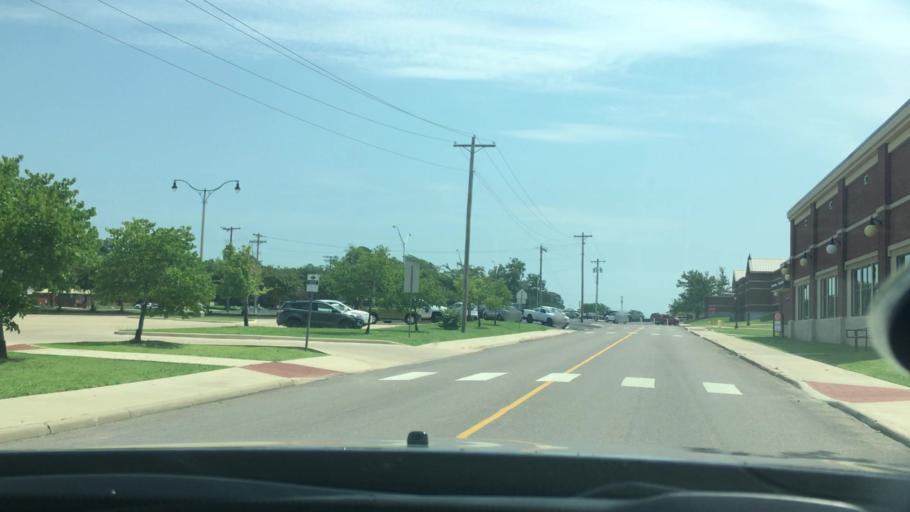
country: US
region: Oklahoma
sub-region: Pontotoc County
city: Ada
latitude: 34.7756
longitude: -96.6667
